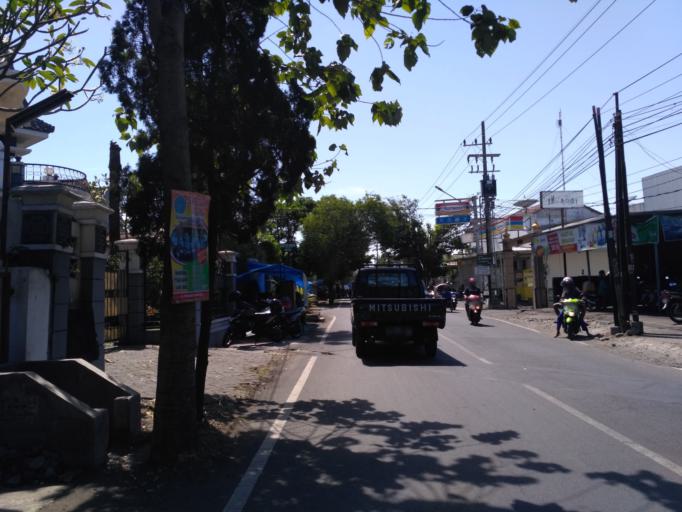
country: ID
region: East Java
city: Malang
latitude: -7.9840
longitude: 112.6470
